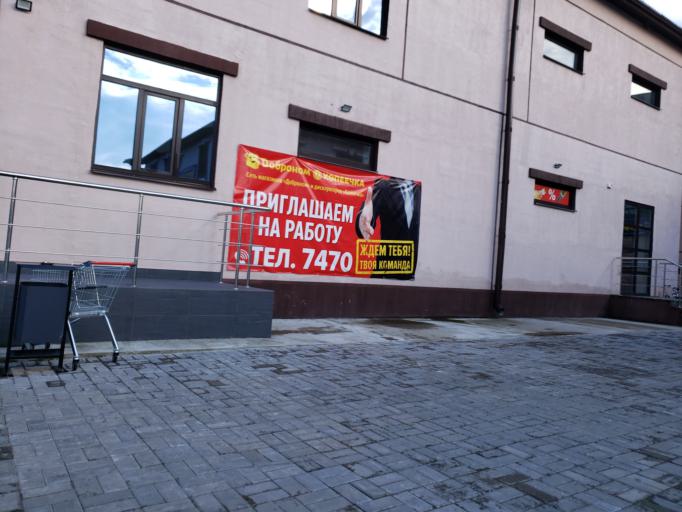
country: BY
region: Minsk
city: Chervyen'
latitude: 53.7057
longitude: 28.4345
